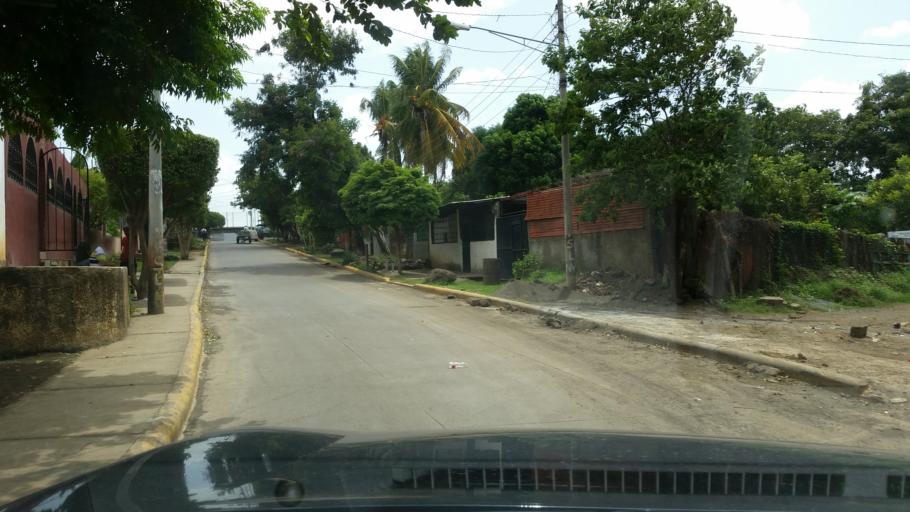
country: NI
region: Managua
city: Managua
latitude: 12.1077
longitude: -86.2223
